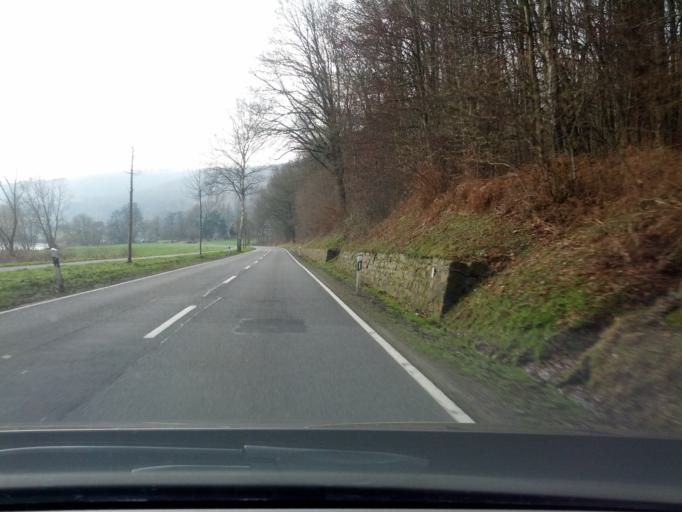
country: DE
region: Lower Saxony
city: Buhren
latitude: 51.5225
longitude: 9.5864
